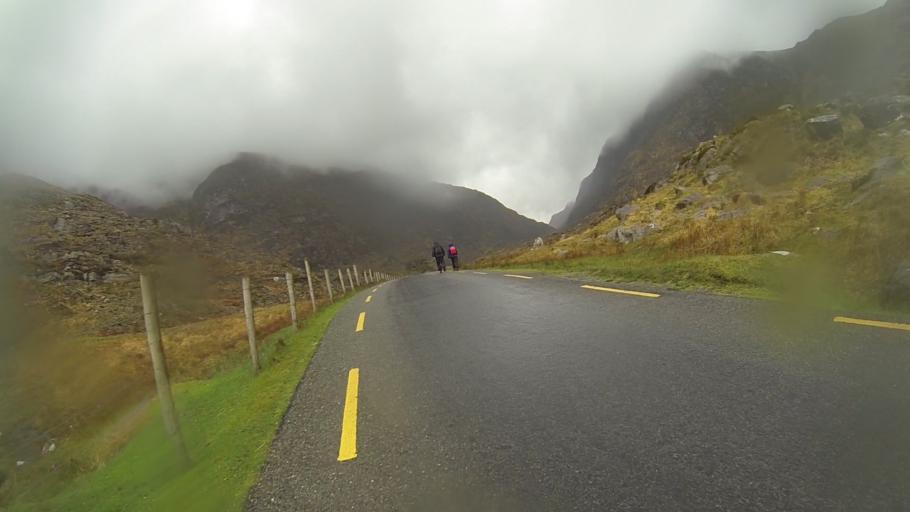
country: IE
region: Munster
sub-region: Ciarrai
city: Cill Airne
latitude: 52.0196
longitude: -9.6360
